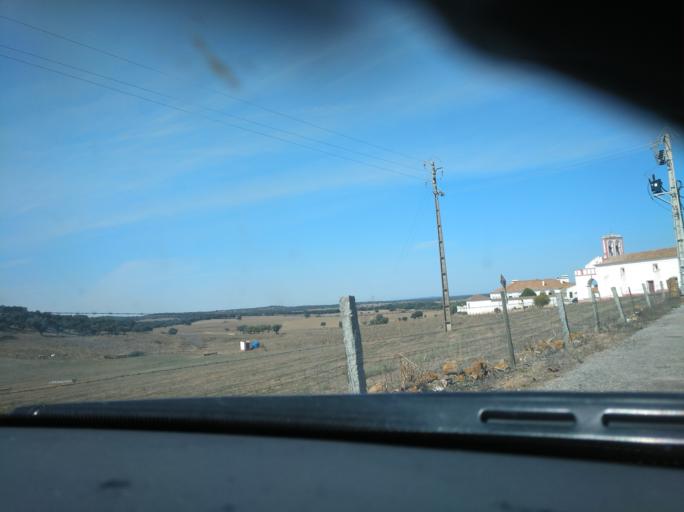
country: PT
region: Evora
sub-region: Arraiolos
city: Arraiolos
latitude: 38.7079
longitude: -8.0996
